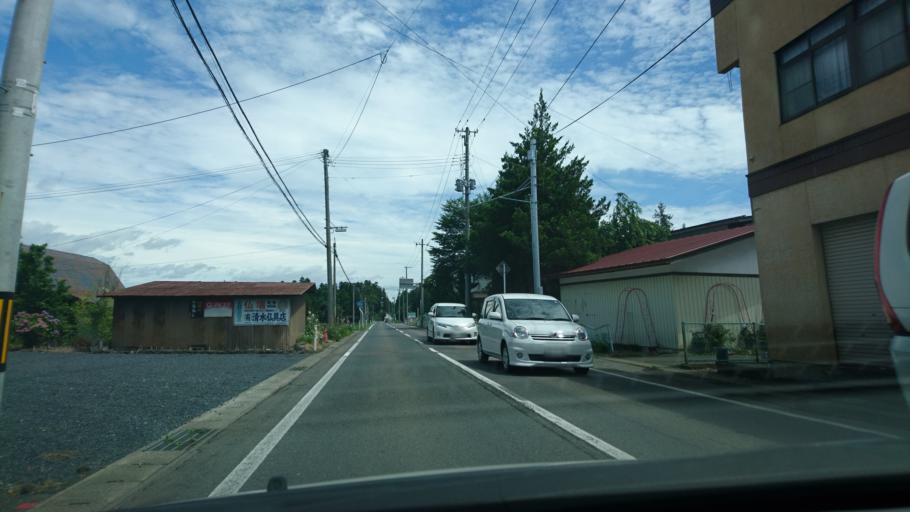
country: JP
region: Iwate
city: Hanamaki
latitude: 39.4057
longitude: 141.1676
